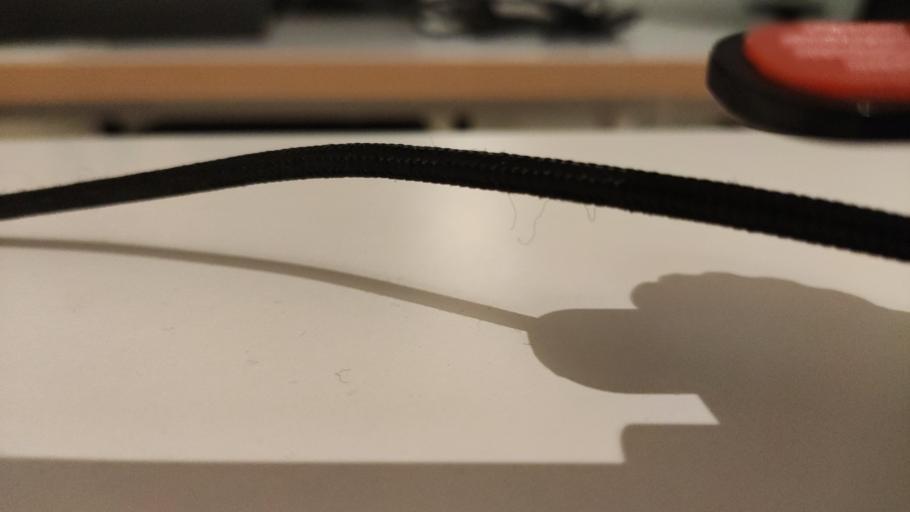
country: RU
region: Moskovskaya
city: Budenovetc
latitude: 56.3713
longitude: 37.5761
